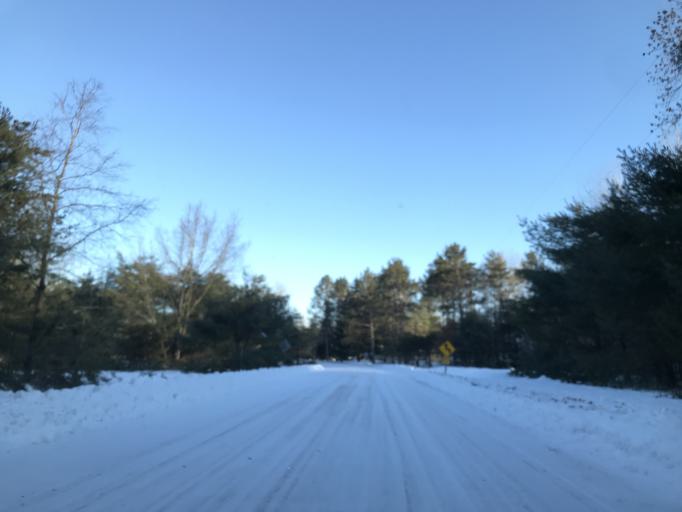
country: US
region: Michigan
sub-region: Menominee County
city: Menominee
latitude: 45.2909
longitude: -87.6956
